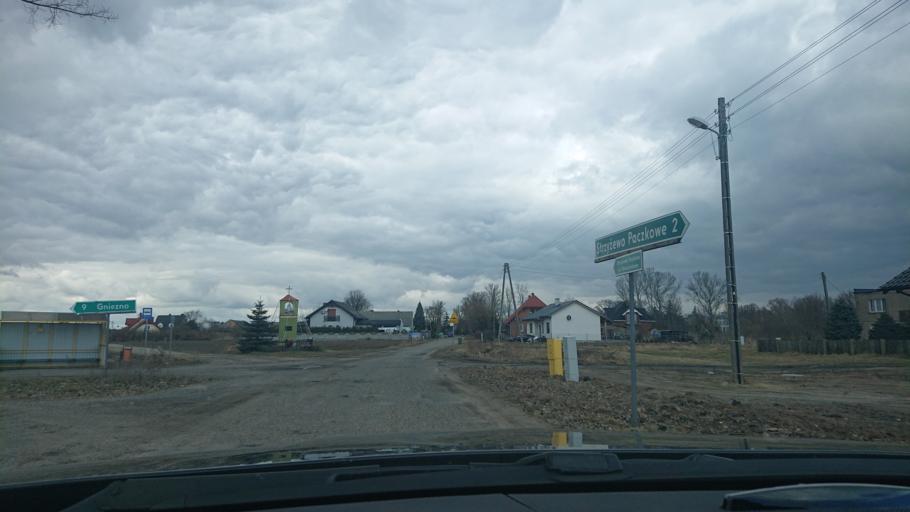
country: PL
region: Greater Poland Voivodeship
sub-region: Powiat gnieznienski
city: Niechanowo
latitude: 52.5884
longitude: 17.6985
